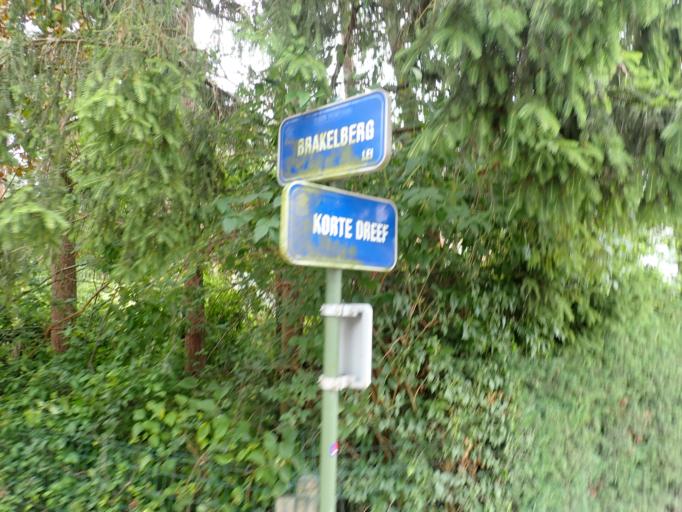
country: BE
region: Flanders
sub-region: Provincie Vlaams-Brabant
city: Boortmeerbeek
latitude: 51.0075
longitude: 4.5881
